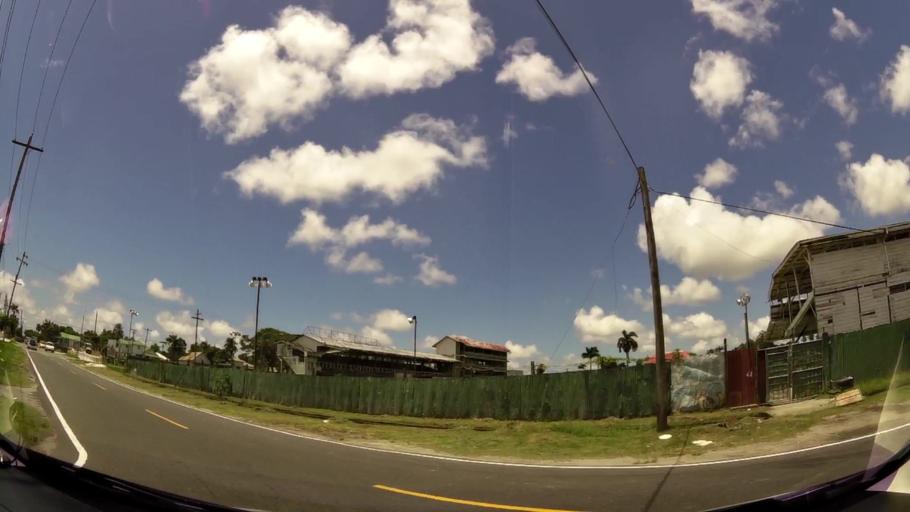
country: GY
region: Demerara-Mahaica
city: Georgetown
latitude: 6.8086
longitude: -58.1507
